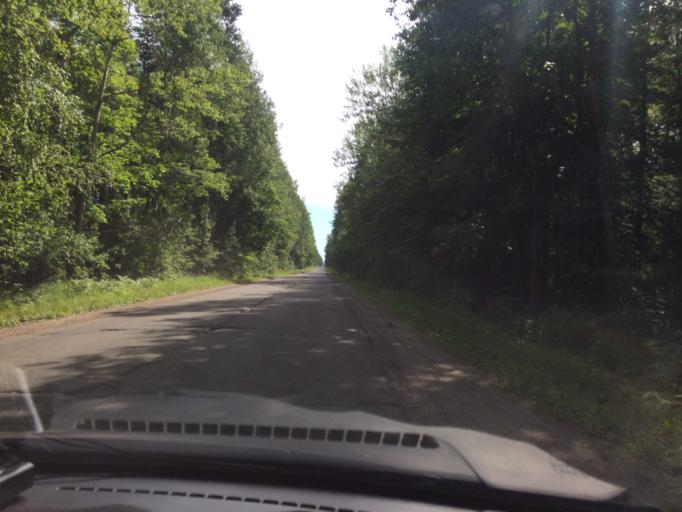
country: RU
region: Mariy-El
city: Surok
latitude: 56.5713
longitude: 48.2123
